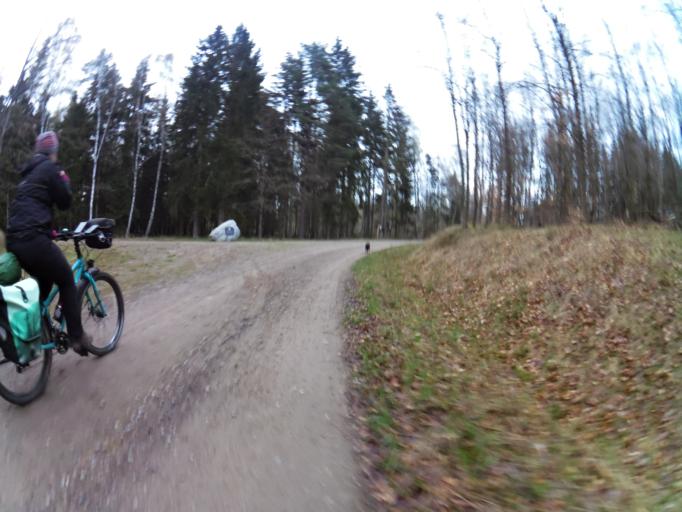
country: PL
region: West Pomeranian Voivodeship
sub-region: Powiat szczecinecki
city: Borne Sulinowo
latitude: 53.6590
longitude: 16.5304
